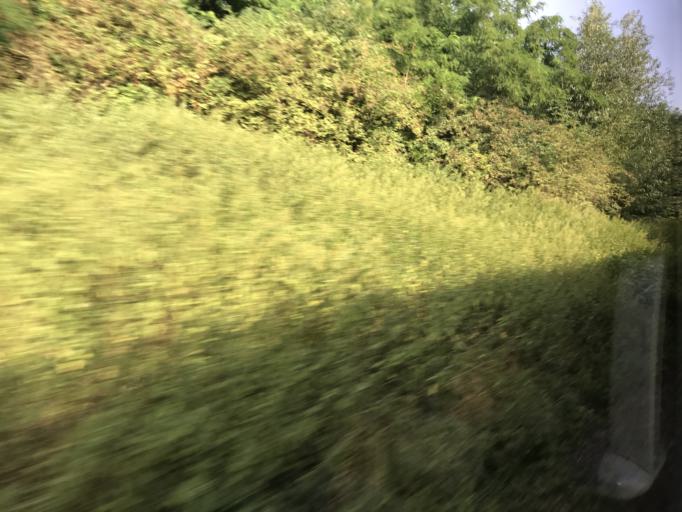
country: DE
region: Hesse
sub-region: Regierungsbezirk Darmstadt
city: Niedernhausen
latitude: 50.0926
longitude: 8.3224
